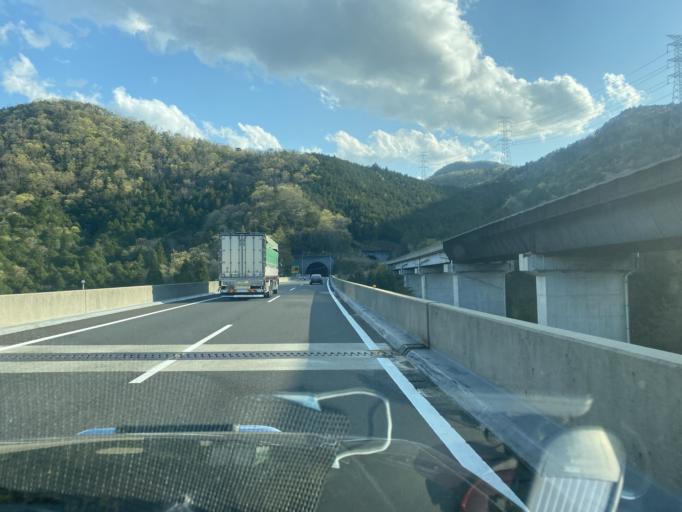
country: JP
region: Hyogo
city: Sasayama
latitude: 34.9827
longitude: 135.1504
